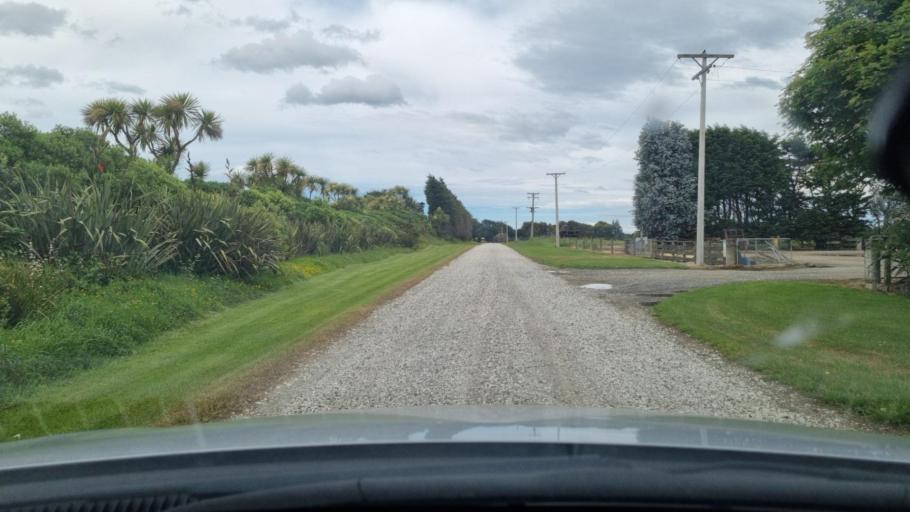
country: NZ
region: Southland
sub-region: Invercargill City
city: Invercargill
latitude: -46.4050
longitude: 168.2600
